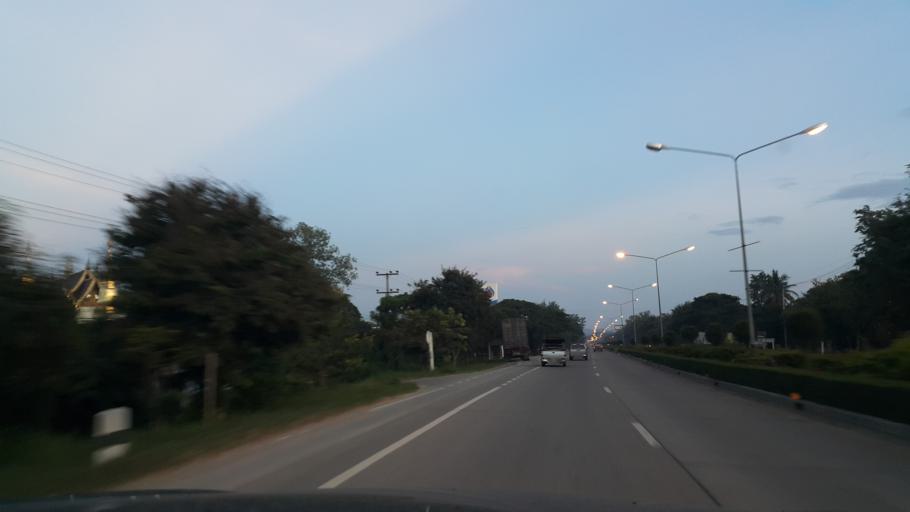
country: TH
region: Lamphun
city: Lamphun
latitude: 18.5680
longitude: 99.0256
